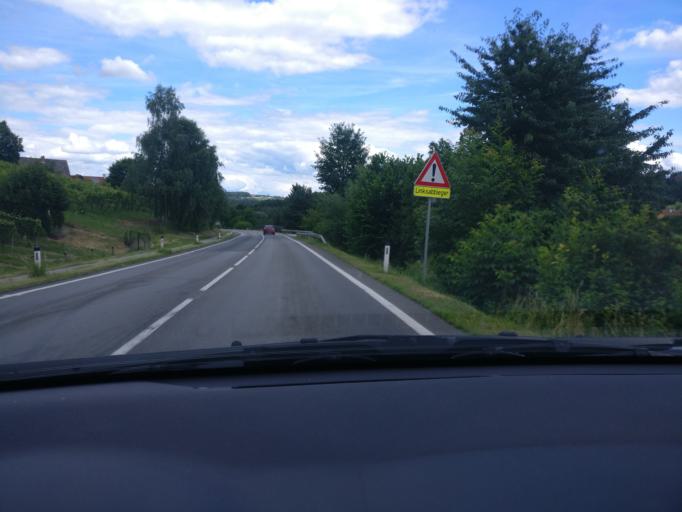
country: AT
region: Styria
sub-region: Politischer Bezirk Weiz
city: Nitscha
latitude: 47.1435
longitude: 15.7625
